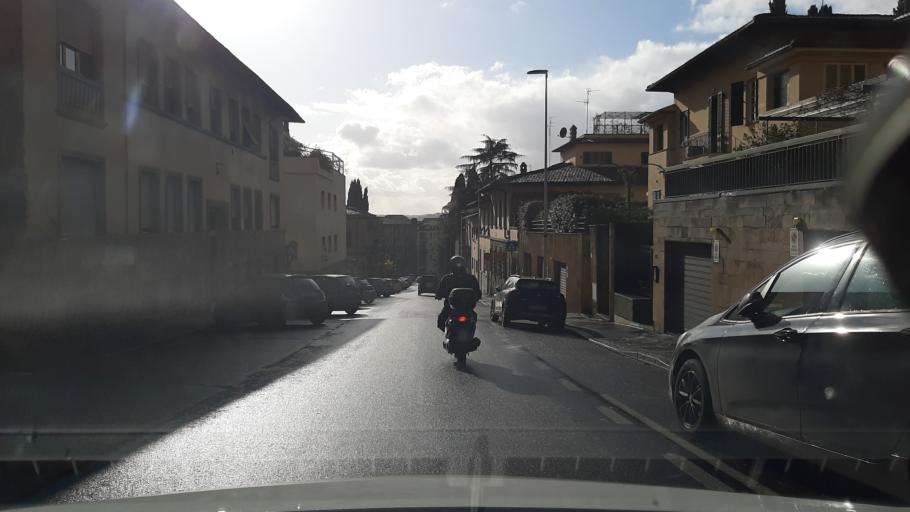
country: IT
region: Tuscany
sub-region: Province of Florence
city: Florence
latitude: 43.7911
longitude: 11.2599
